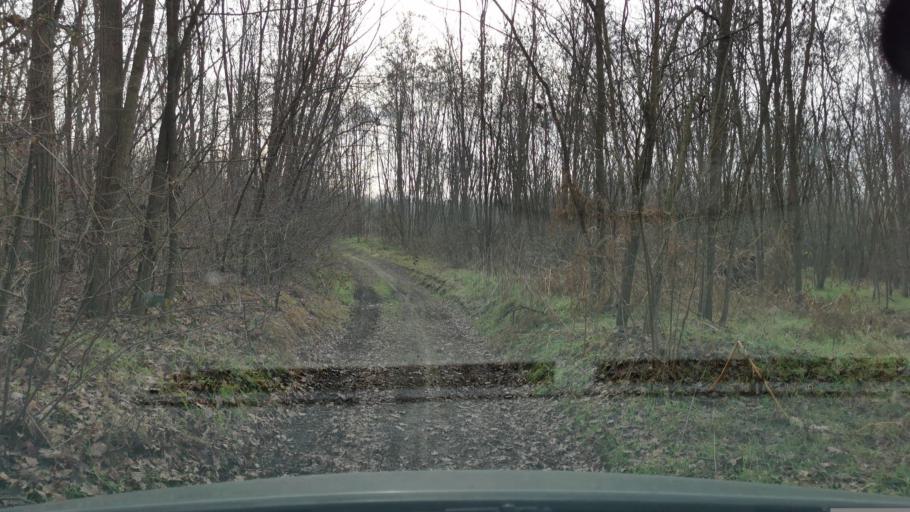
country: IT
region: Piedmont
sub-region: Provincia di Torino
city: San Benigno Canavese
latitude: 45.2547
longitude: 7.7951
